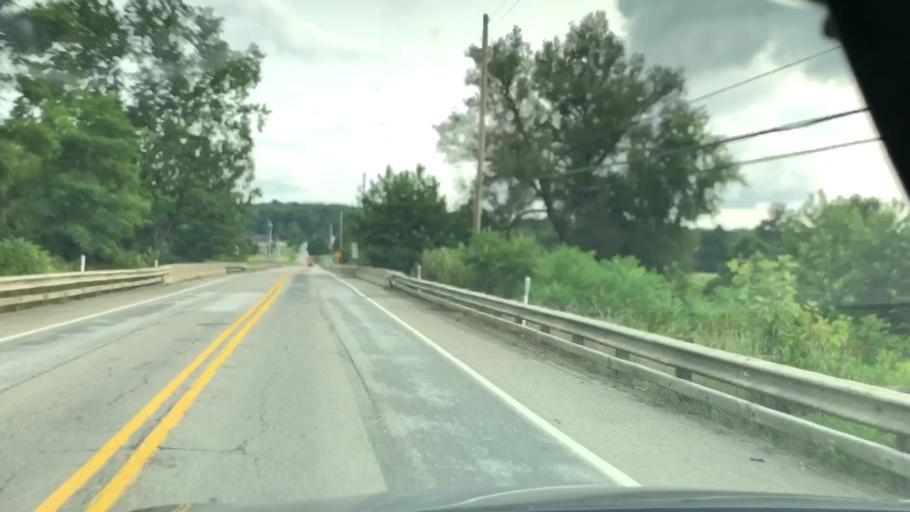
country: US
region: Pennsylvania
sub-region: Erie County
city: Union City
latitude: 41.9984
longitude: -79.8109
